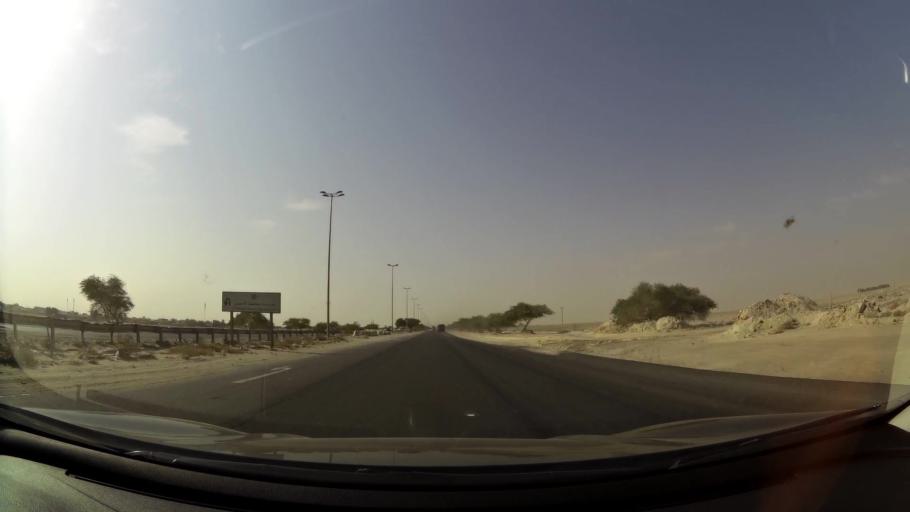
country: KW
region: Al Ahmadi
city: Al Ahmadi
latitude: 28.9467
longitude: 48.1155
